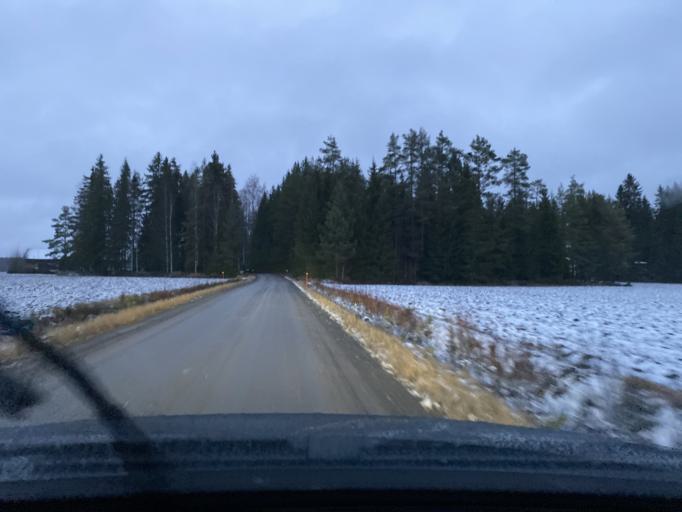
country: FI
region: Pirkanmaa
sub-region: Lounais-Pirkanmaa
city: Punkalaidun
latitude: 61.1607
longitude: 22.9459
